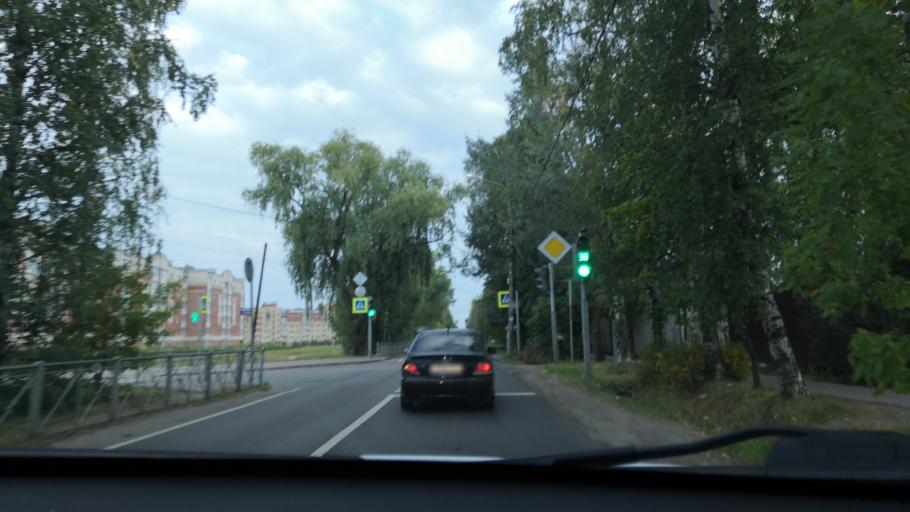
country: RU
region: St.-Petersburg
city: Pushkin
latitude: 59.6996
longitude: 30.4097
